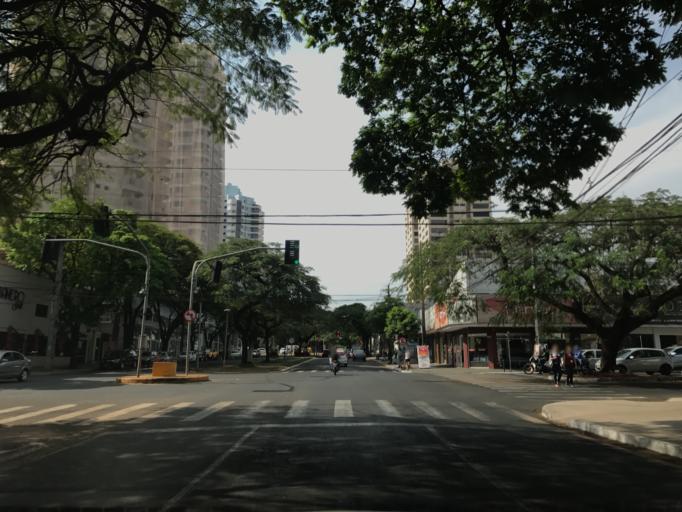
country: BR
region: Parana
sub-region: Maringa
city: Maringa
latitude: -23.4207
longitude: -51.9283
